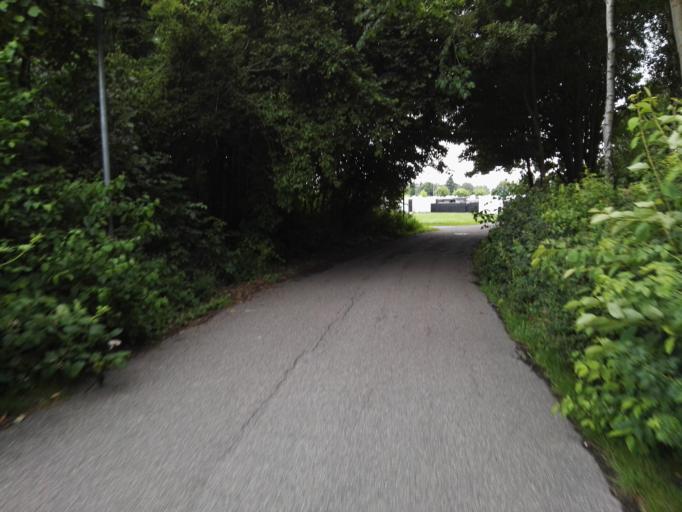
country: DK
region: Capital Region
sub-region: Egedal Kommune
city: Olstykke
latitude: 55.7840
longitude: 12.1729
